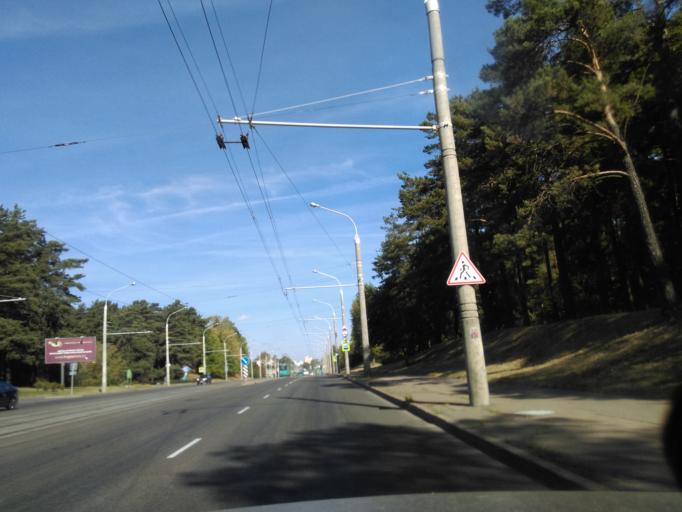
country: BY
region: Minsk
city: Minsk
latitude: 53.8815
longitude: 27.6239
